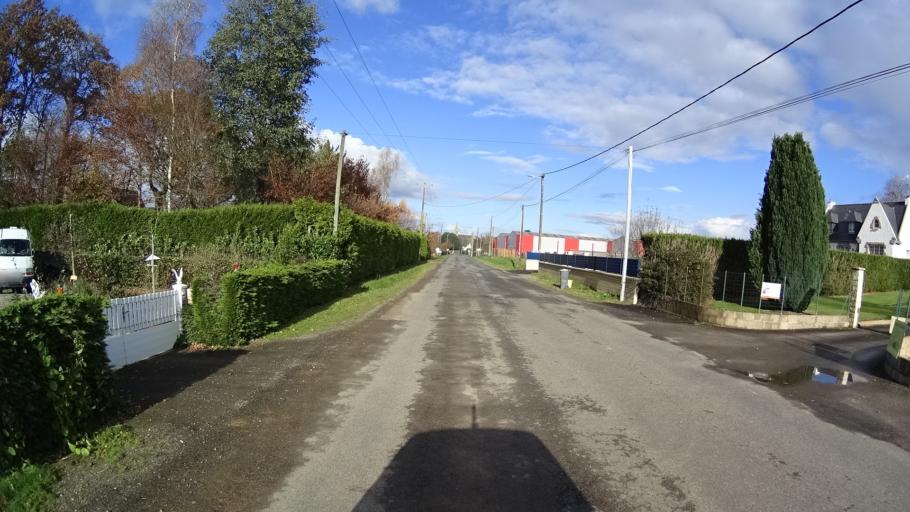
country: FR
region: Brittany
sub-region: Departement du Morbihan
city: Carentoir
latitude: 47.8092
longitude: -2.1324
